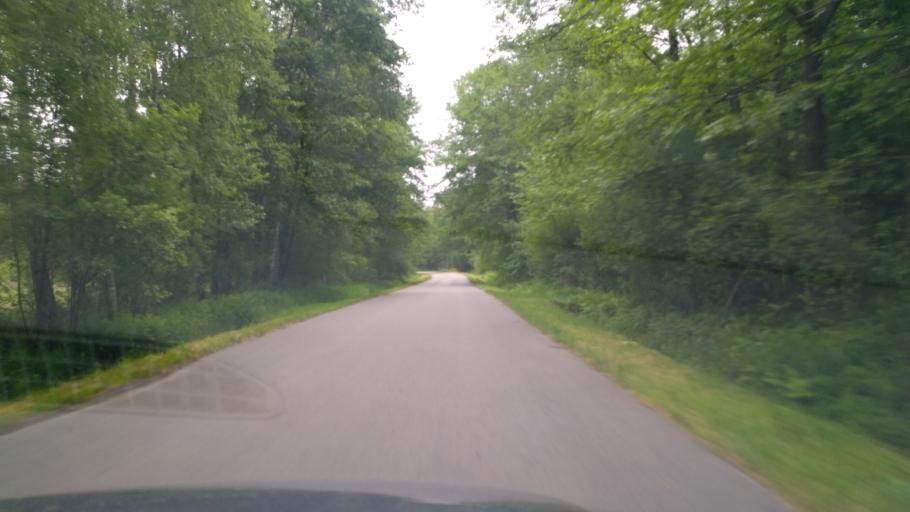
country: PL
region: Subcarpathian Voivodeship
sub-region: Powiat kolbuszowski
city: Niwiska
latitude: 50.2126
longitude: 21.6572
